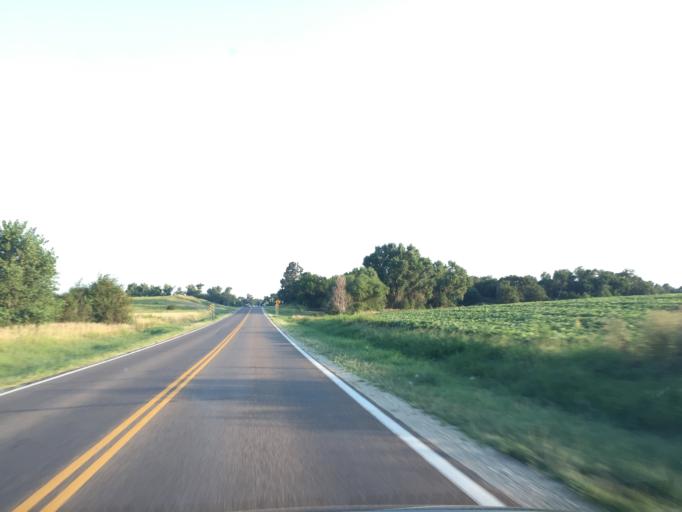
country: US
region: Kansas
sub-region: Ellsworth County
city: Ellsworth
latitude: 38.7452
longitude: -98.2252
